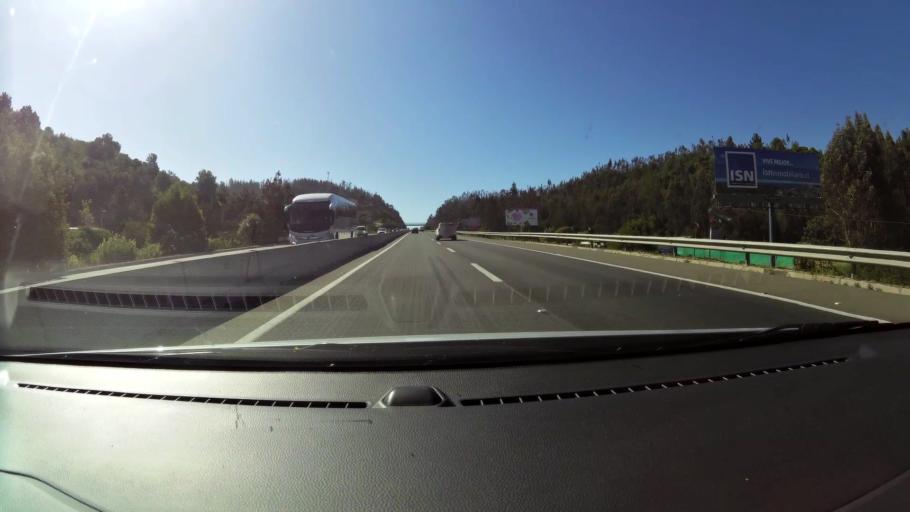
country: CL
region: Valparaiso
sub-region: Provincia de Marga Marga
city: Quilpue
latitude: -33.2124
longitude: -71.4766
